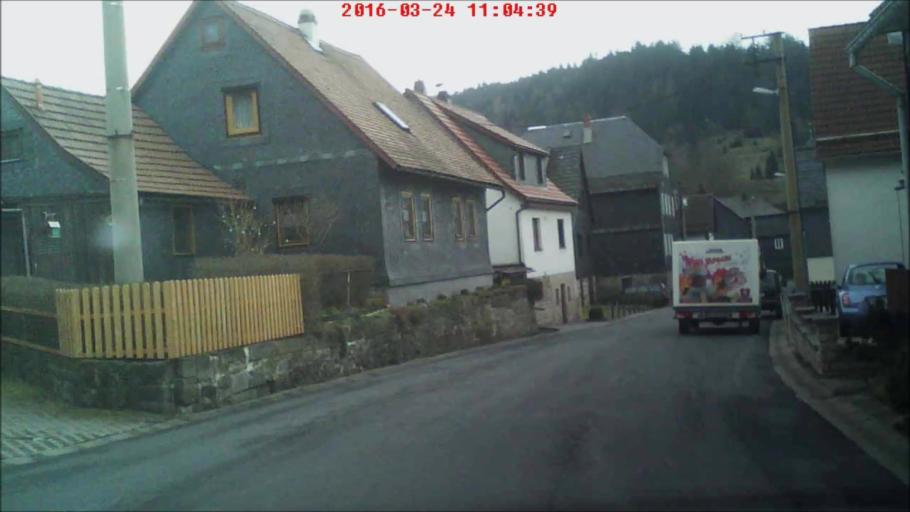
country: DE
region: Thuringia
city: Neustadt am Rennsteig
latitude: 50.5393
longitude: 10.9206
